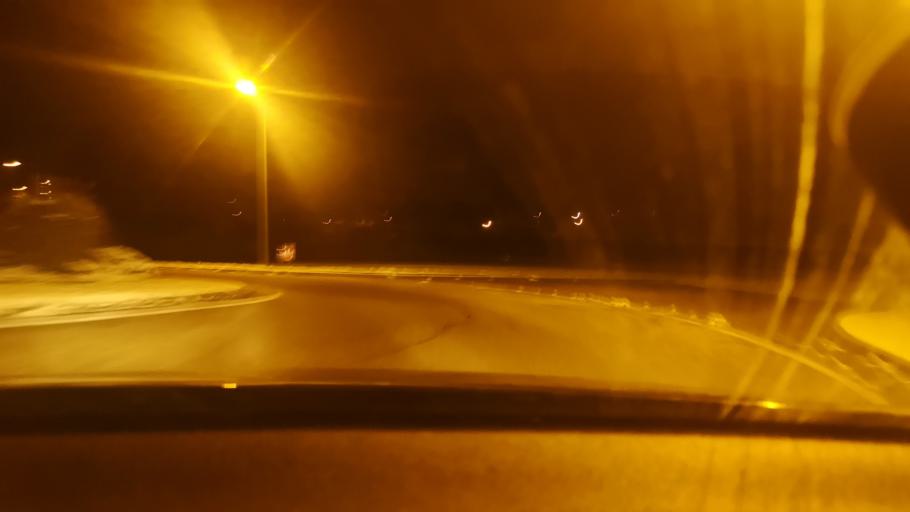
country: FR
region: Rhone-Alpes
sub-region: Departement de l'Ain
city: Ceyzeriat
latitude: 46.1767
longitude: 5.3302
